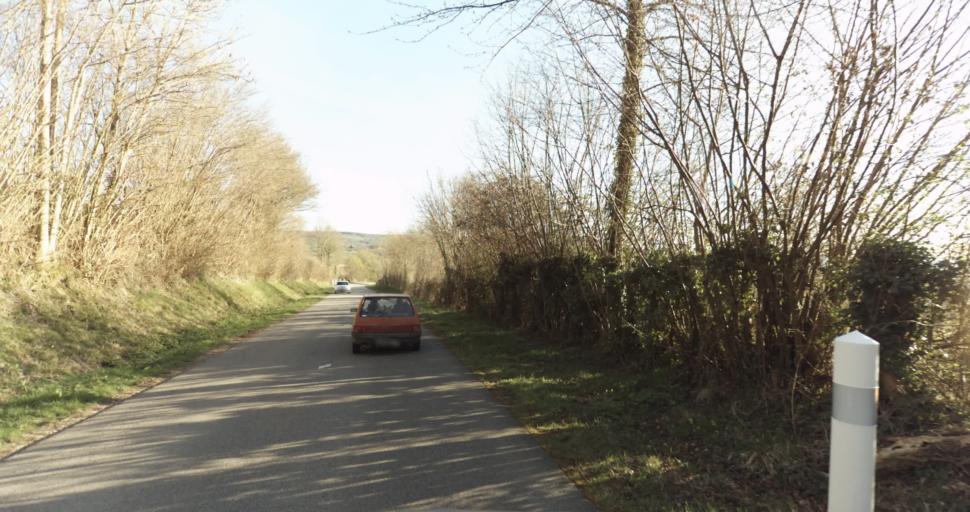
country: FR
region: Lower Normandy
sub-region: Departement du Calvados
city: Livarot
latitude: 48.9662
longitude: 0.0680
